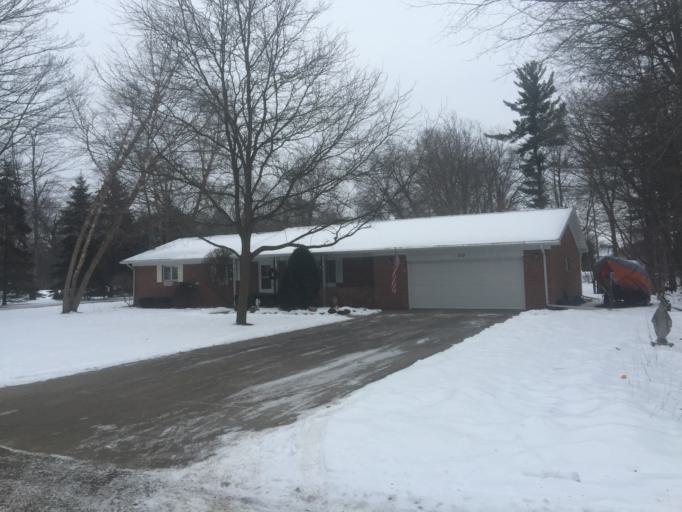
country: US
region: Wisconsin
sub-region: Marinette County
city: Peshtigo
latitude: 45.2367
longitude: -88.0031
